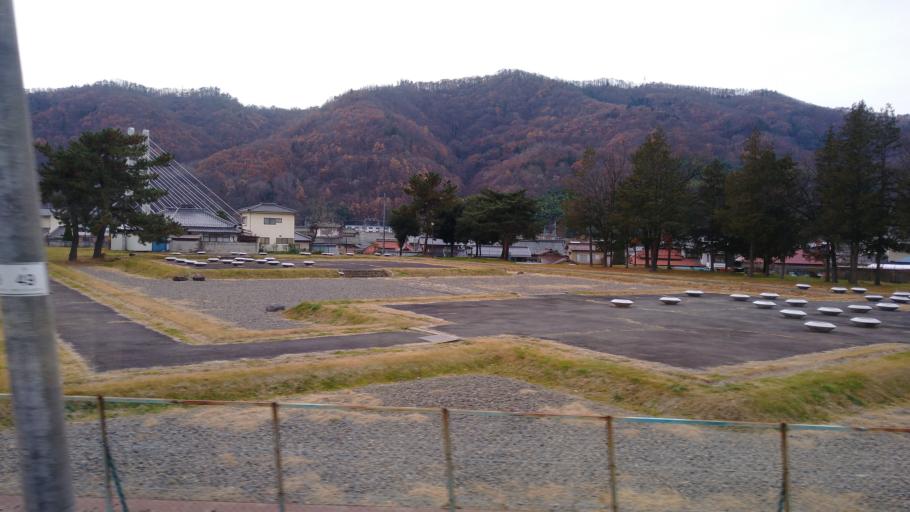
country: JP
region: Nagano
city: Ueda
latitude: 36.3808
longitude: 138.2694
